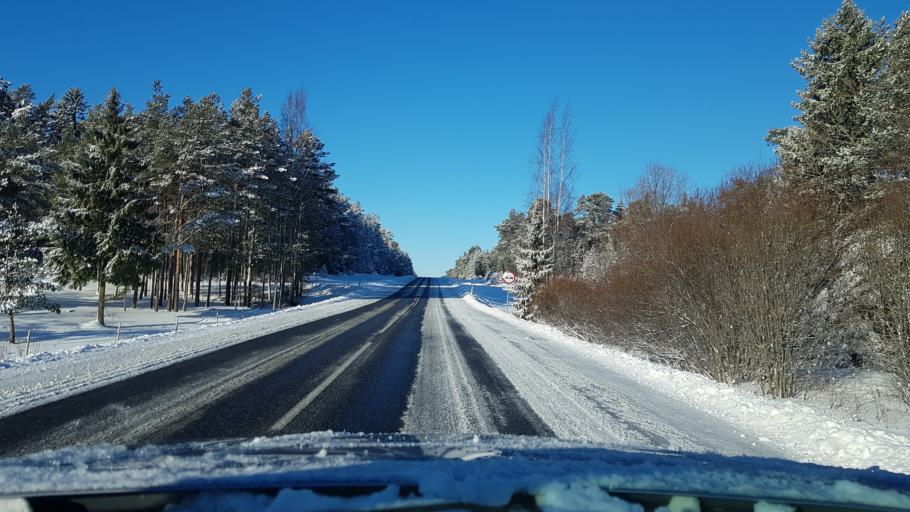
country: EE
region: Hiiumaa
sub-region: Kaerdla linn
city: Kardla
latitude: 58.9584
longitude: 22.8577
